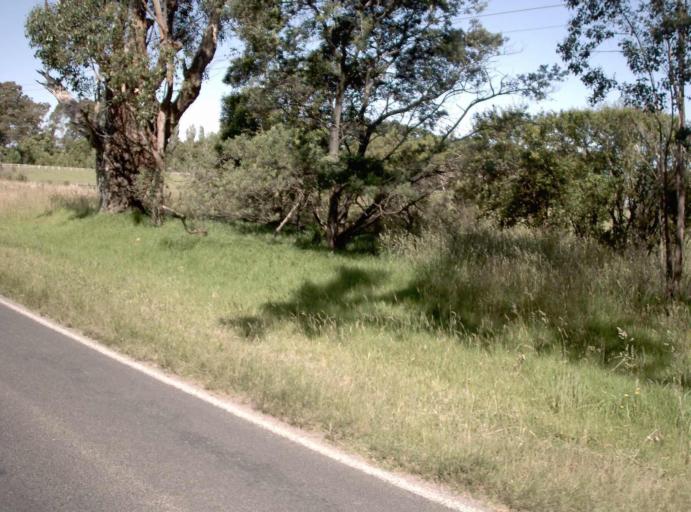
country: AU
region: Victoria
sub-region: Latrobe
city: Morwell
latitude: -38.6448
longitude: 146.4792
